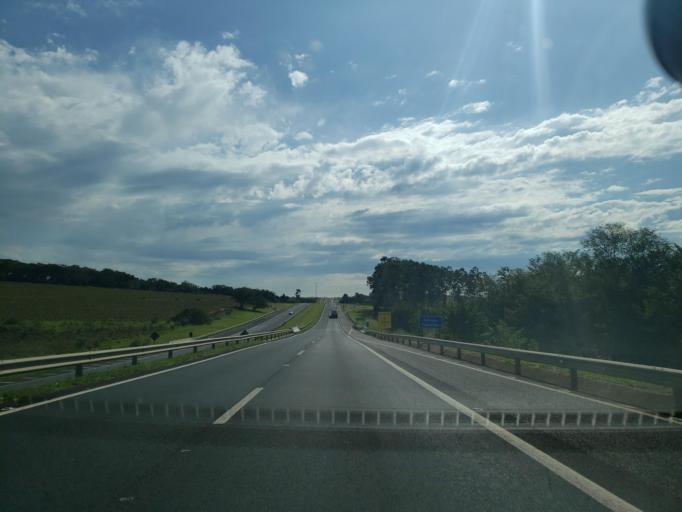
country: BR
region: Sao Paulo
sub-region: Cafelandia
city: Cafelandia
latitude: -21.8956
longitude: -49.5354
